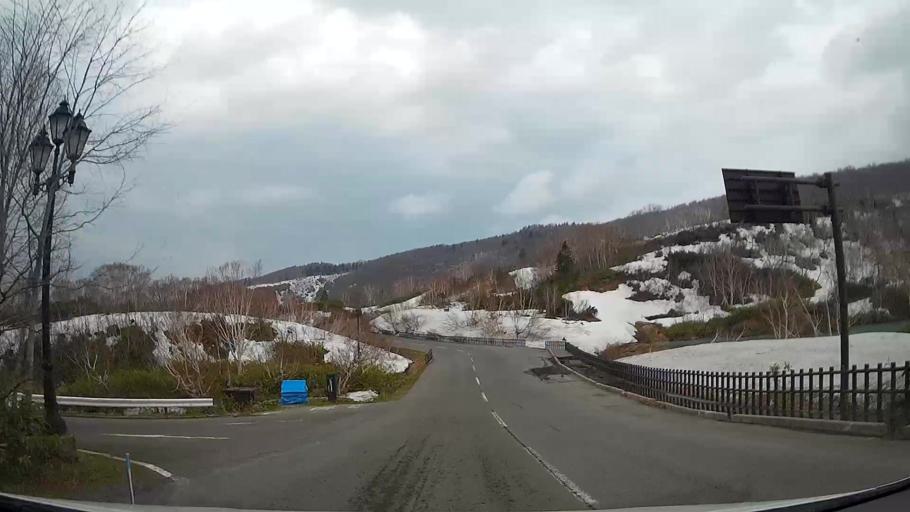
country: JP
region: Aomori
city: Aomori Shi
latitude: 40.6466
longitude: 140.8541
